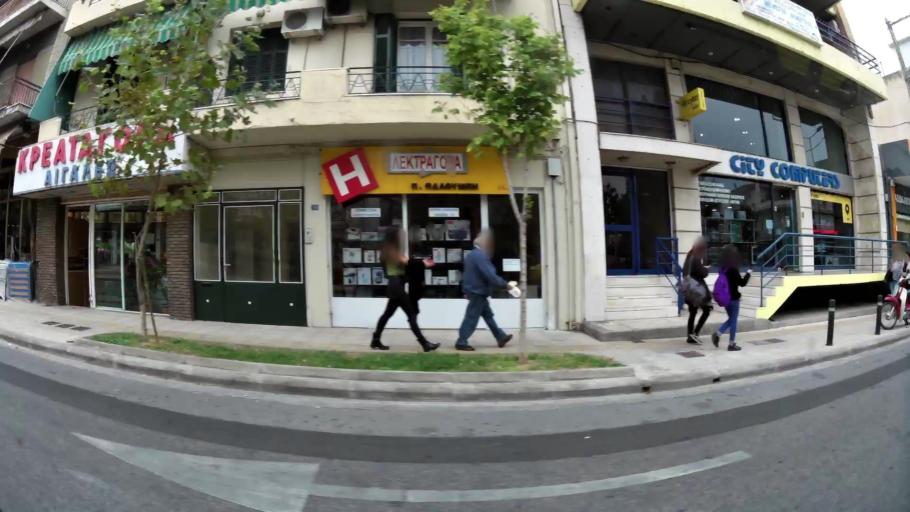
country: GR
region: Attica
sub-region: Nomarchia Athinas
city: Aigaleo
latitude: 37.9900
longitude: 23.6768
